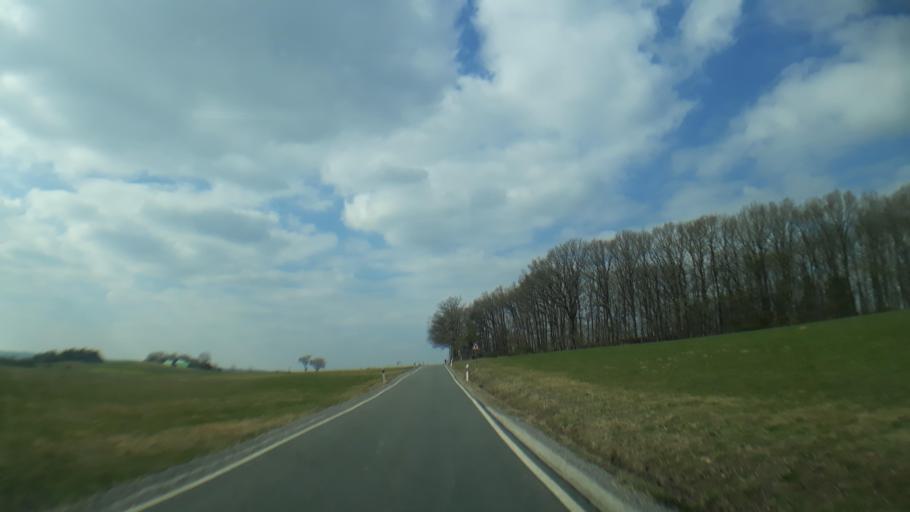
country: DE
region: Rheinland-Pfalz
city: Berg
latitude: 50.5519
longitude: 6.9224
